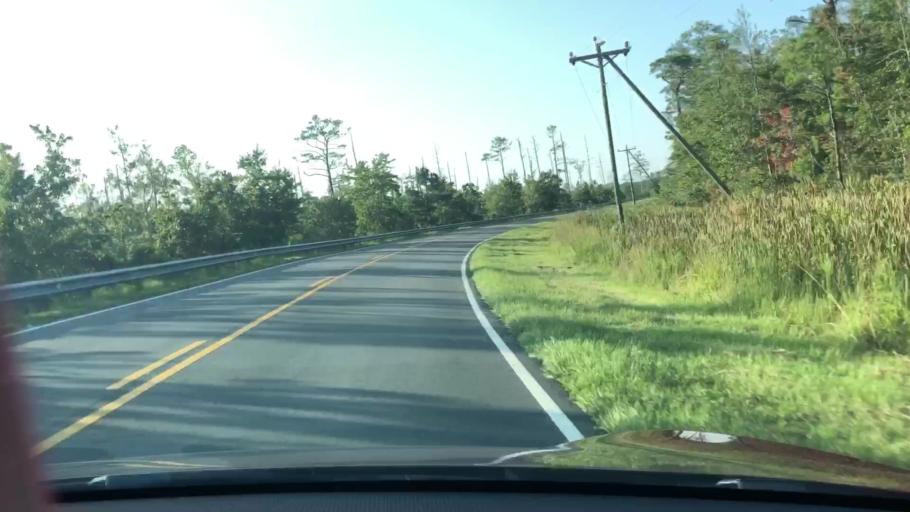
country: US
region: North Carolina
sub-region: Dare County
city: Manteo
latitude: 35.8317
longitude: -75.8101
